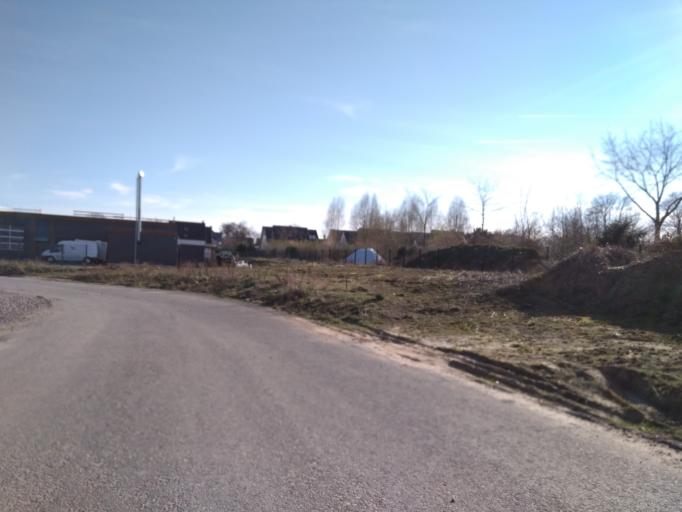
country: DE
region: North Rhine-Westphalia
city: Dorsten
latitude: 51.6124
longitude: 6.9224
